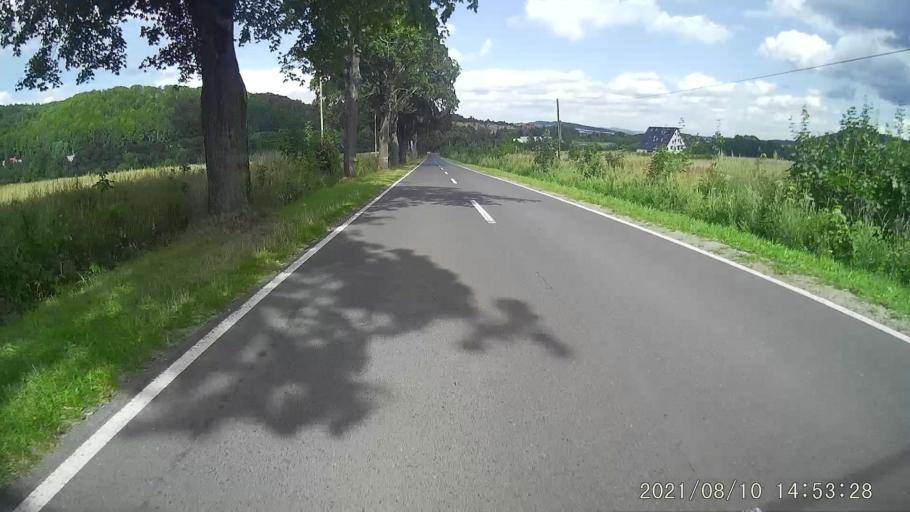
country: PL
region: Lower Silesian Voivodeship
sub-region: Powiat klodzki
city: Radkow
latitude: 50.4962
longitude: 16.3764
